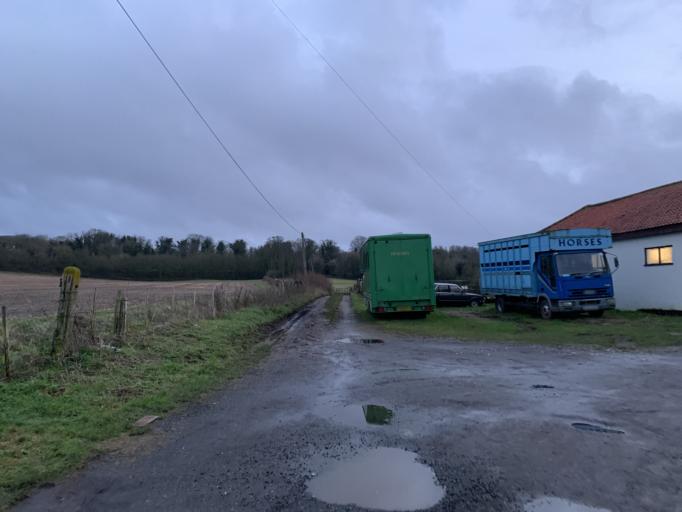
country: GB
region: England
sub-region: Kent
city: Eynsford
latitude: 51.3633
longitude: 0.1991
